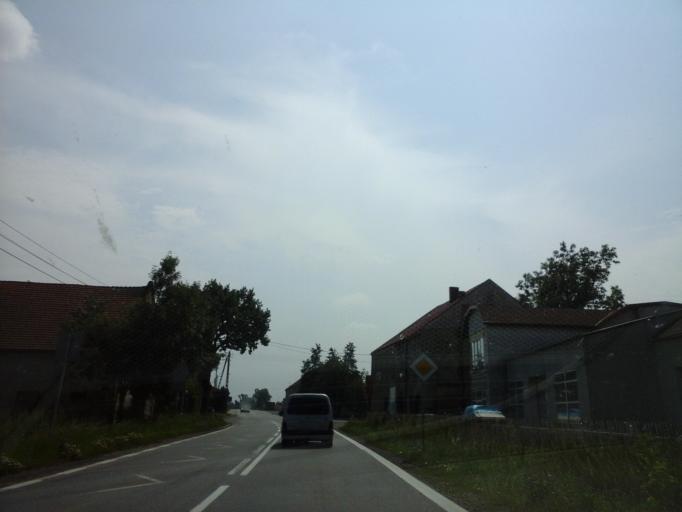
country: PL
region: Lower Silesian Voivodeship
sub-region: Powiat wroclawski
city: Zorawina
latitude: 50.9813
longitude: 17.0698
